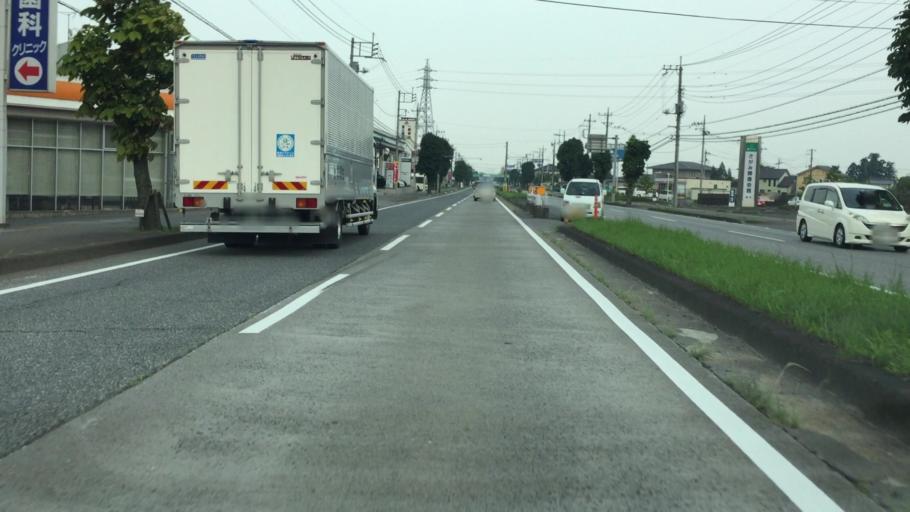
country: JP
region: Tochigi
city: Tochigi
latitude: 36.4015
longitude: 139.7142
